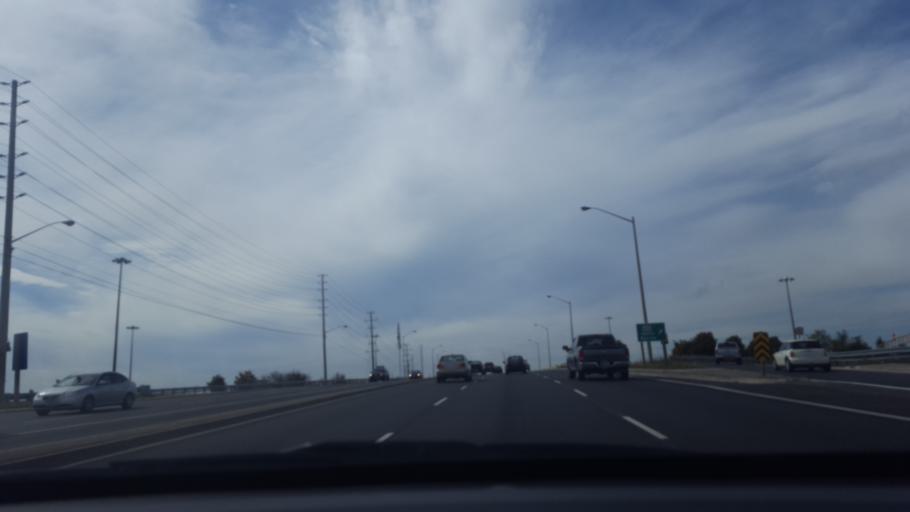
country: CA
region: Ontario
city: Vaughan
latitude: 43.8286
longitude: -79.5439
